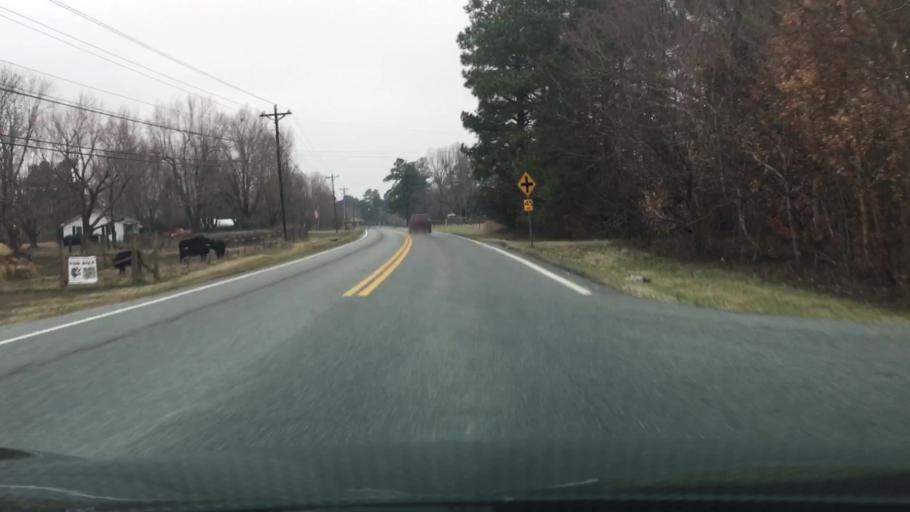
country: US
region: Kentucky
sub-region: Marshall County
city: Calvert City
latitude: 36.9708
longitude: -88.4162
